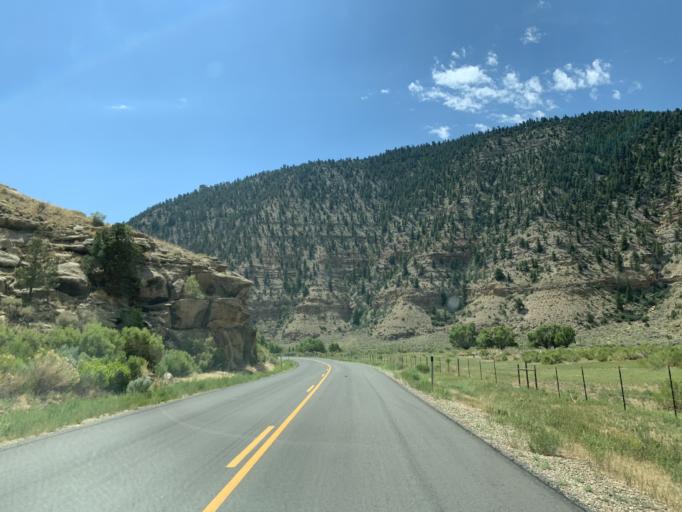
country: US
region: Utah
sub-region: Carbon County
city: East Carbon City
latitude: 39.8018
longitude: -110.3706
